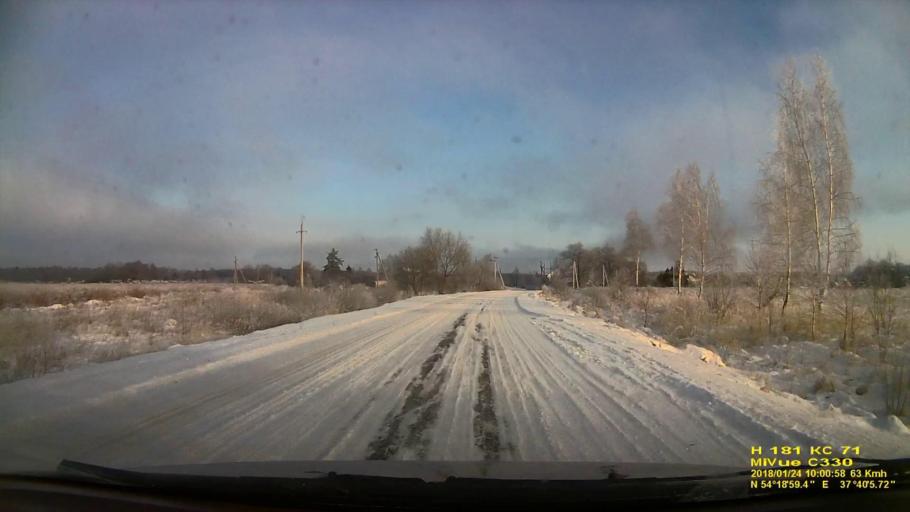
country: RU
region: Tula
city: Revyakino
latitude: 54.3166
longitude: 37.6683
